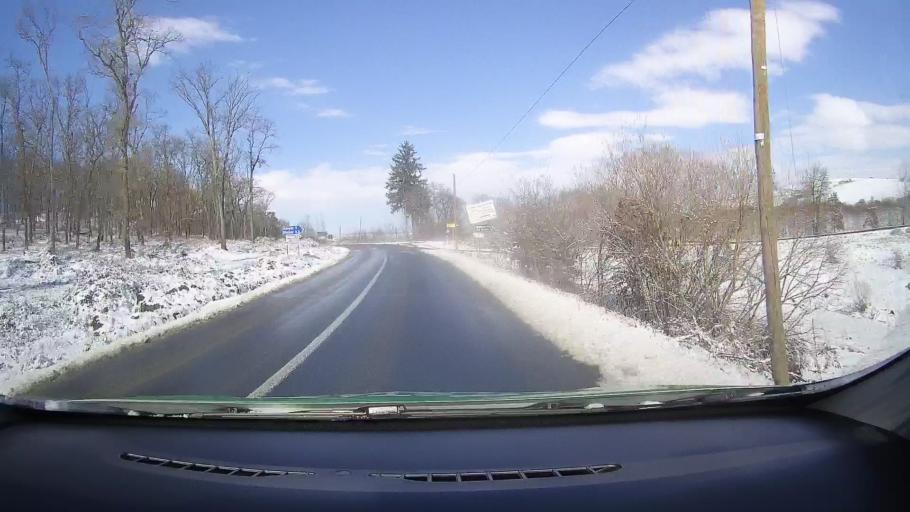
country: RO
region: Sibiu
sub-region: Comuna Nocrich
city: Nocrich
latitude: 45.8648
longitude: 24.4545
